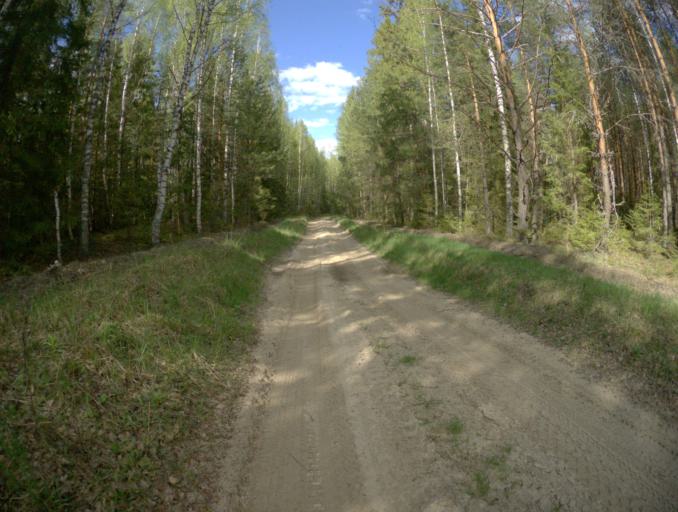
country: RU
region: Vladimir
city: Golovino
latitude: 55.8906
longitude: 40.4091
